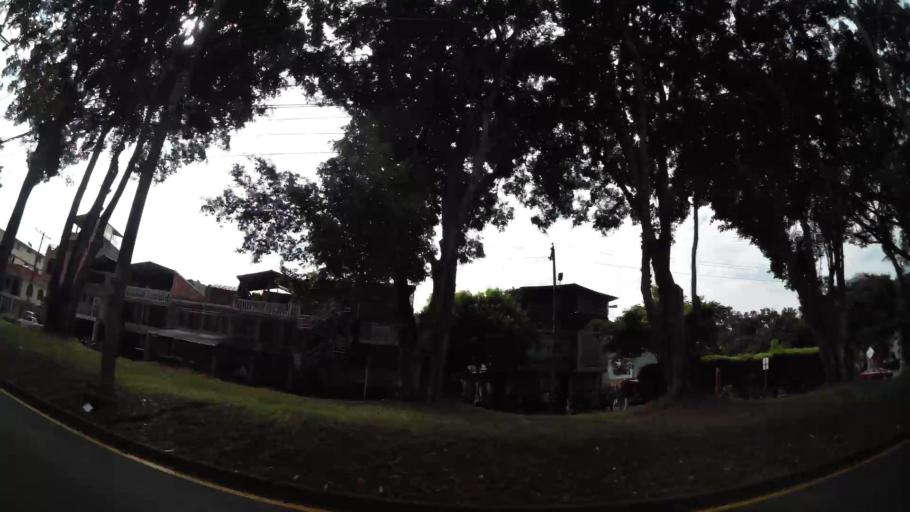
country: CO
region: Valle del Cauca
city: Cali
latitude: 3.4813
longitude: -76.4928
